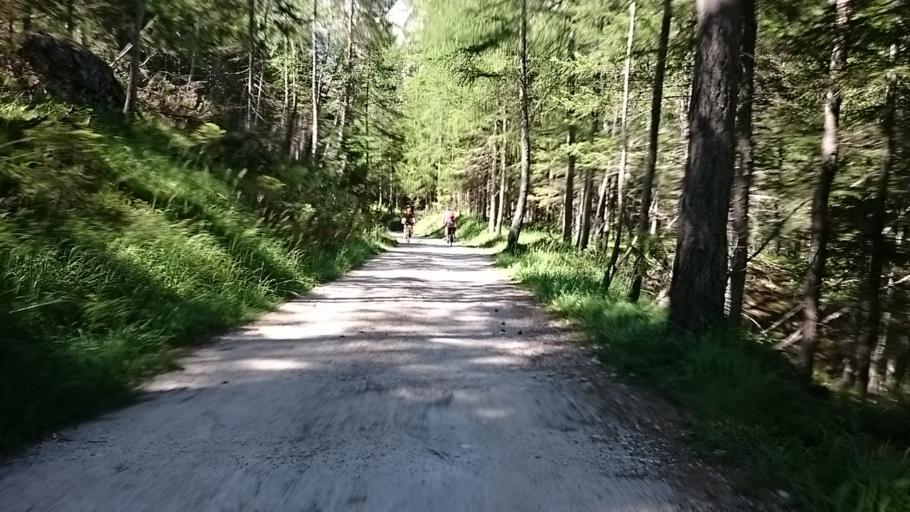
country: IT
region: Veneto
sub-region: Provincia di Belluno
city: Cortina d'Ampezzo
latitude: 46.5947
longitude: 12.1157
